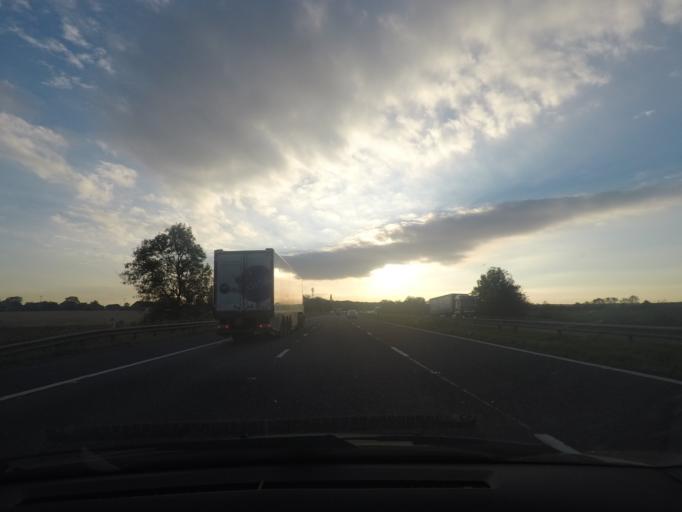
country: GB
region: England
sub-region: North Lincolnshire
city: Brigg
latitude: 53.5547
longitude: -0.5101
